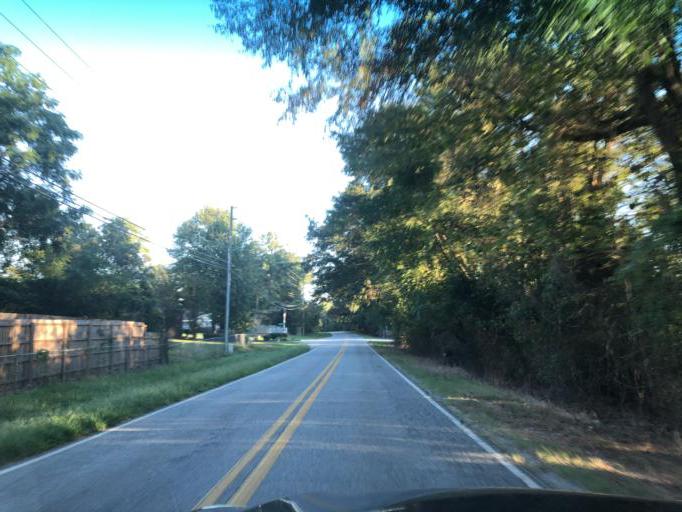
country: US
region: Georgia
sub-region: Muscogee County
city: Columbus
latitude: 32.5388
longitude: -84.8936
